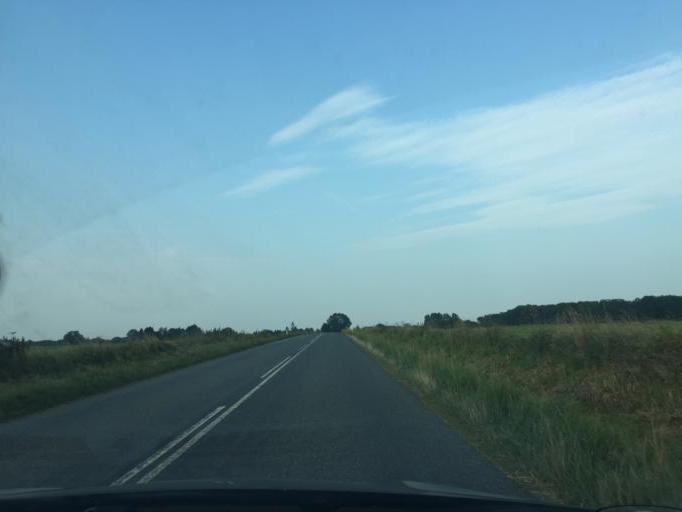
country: DK
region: South Denmark
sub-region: Kerteminde Kommune
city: Langeskov
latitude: 55.3003
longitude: 10.5749
